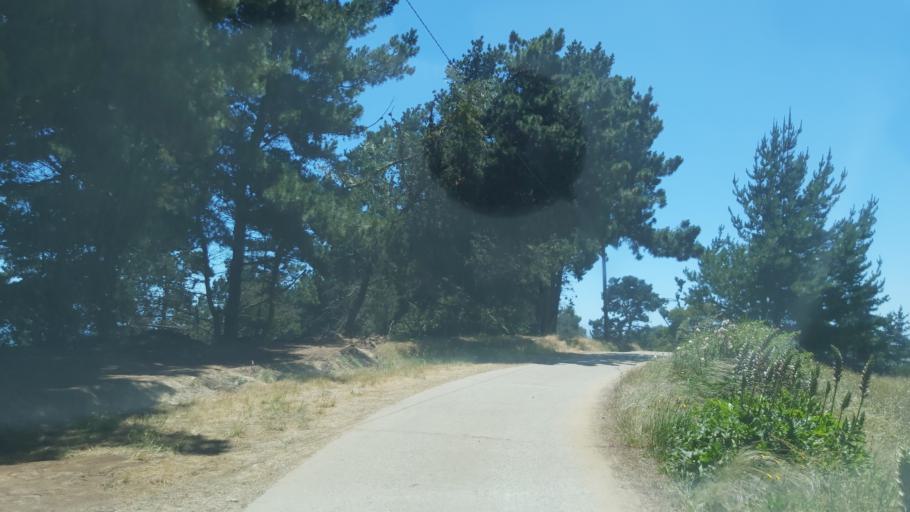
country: CL
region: Maule
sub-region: Provincia de Talca
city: Constitucion
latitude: -35.3224
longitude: -72.4131
